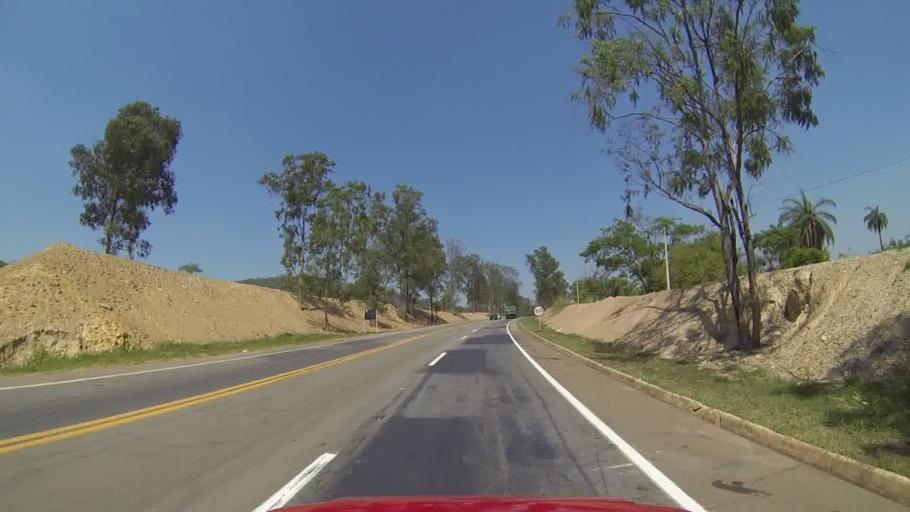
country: BR
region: Minas Gerais
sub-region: Mateus Leme
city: Mateus Leme
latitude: -20.0254
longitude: -44.5045
